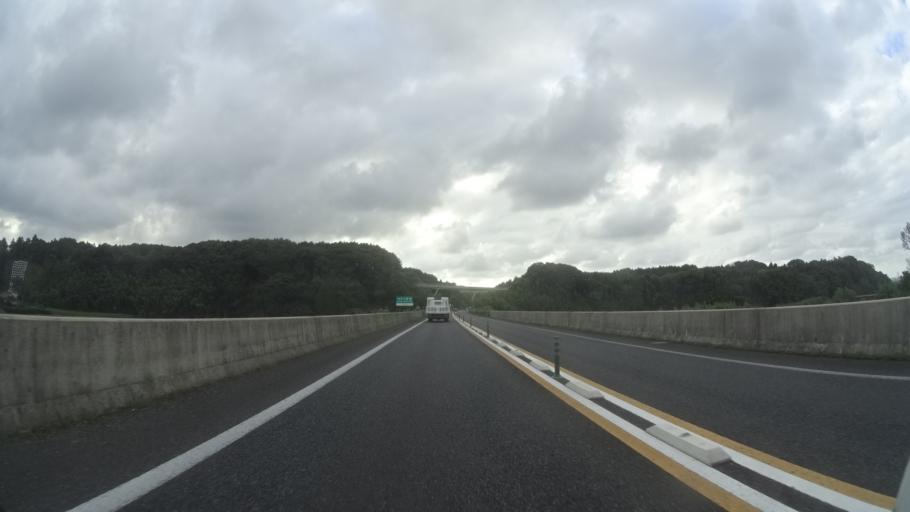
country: JP
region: Tottori
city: Kurayoshi
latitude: 35.4850
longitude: 133.6883
